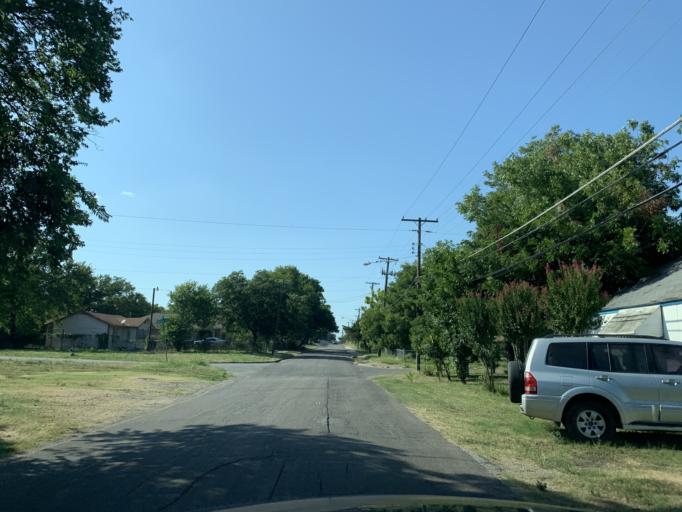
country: US
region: Texas
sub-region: Dallas County
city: Dallas
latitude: 32.7023
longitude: -96.7938
